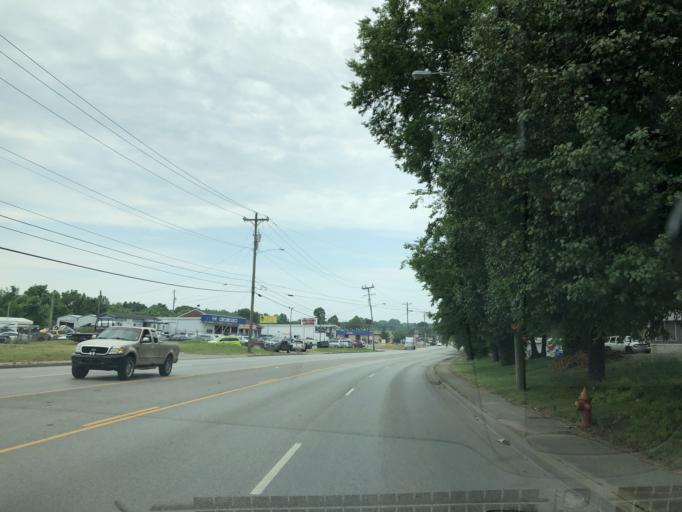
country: US
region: Tennessee
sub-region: Davidson County
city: Oak Hill
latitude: 36.0744
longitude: -86.6819
